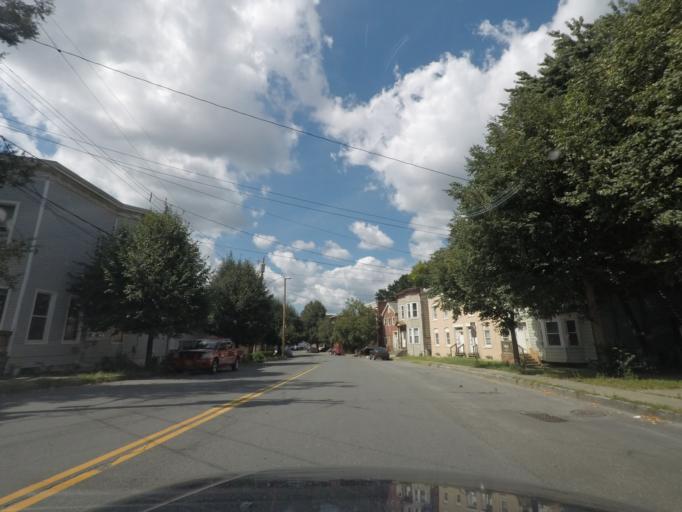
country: US
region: New York
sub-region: Rensselaer County
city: Troy
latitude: 42.7197
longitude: -73.6855
